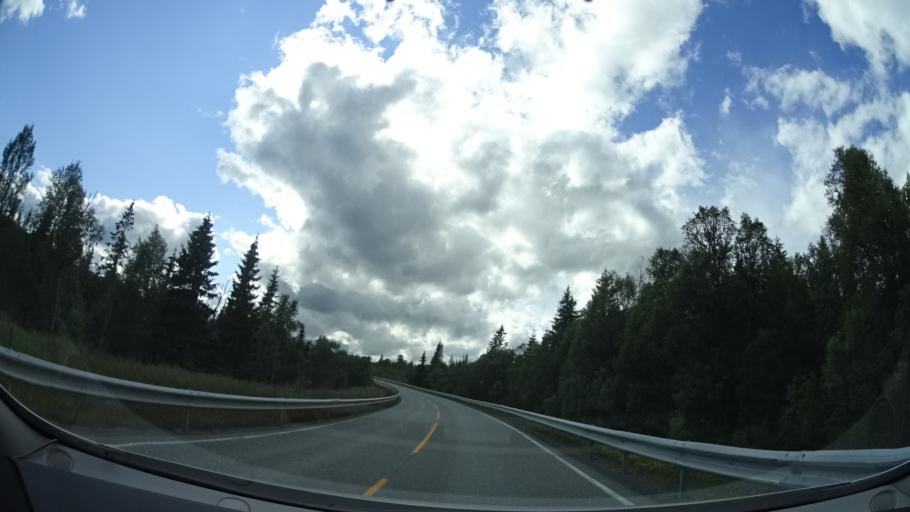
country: NO
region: Sor-Trondelag
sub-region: Snillfjord
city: Krokstadora
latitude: 63.2325
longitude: 9.4521
